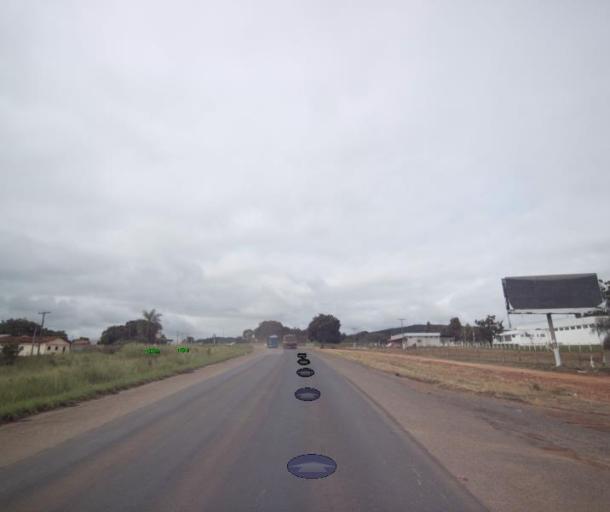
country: BR
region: Goias
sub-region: Uruacu
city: Uruacu
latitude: -14.5390
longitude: -49.1622
